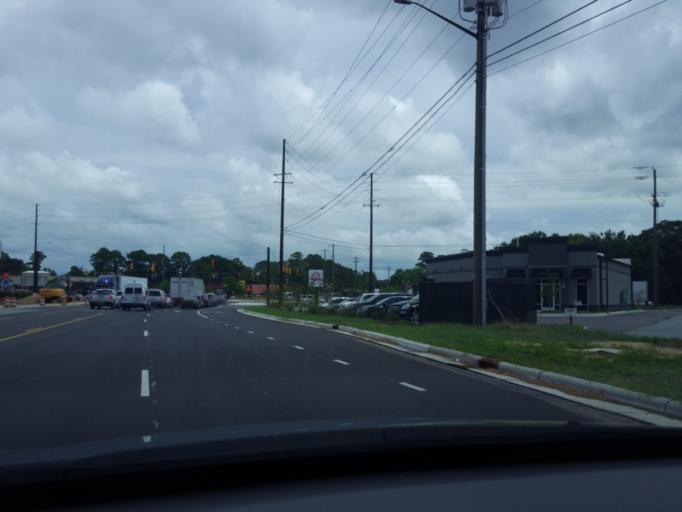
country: US
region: North Carolina
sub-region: Pitt County
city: Greenville
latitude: 35.6073
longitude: -77.3965
